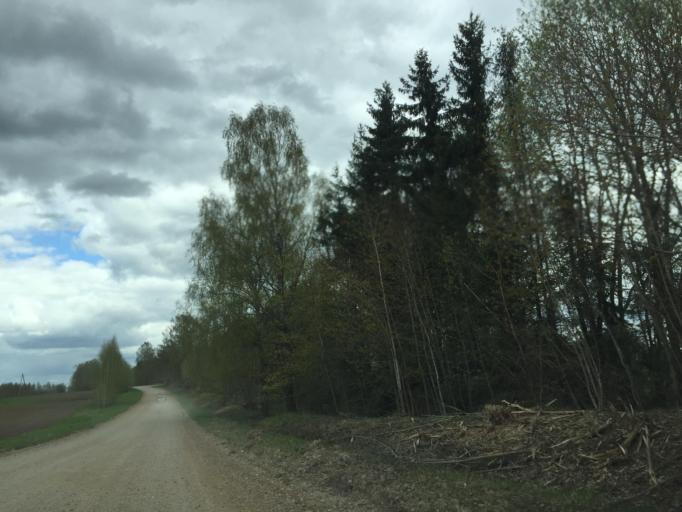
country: LV
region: Madonas Rajons
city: Madona
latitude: 56.9254
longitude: 26.0353
